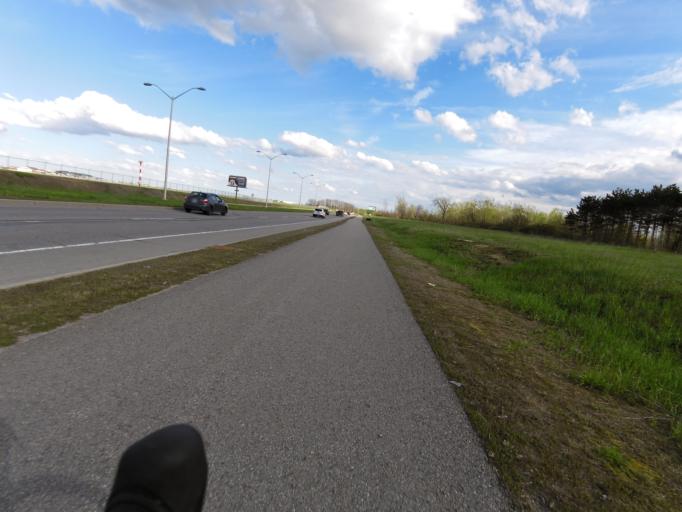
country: CA
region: Ontario
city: Ottawa
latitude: 45.3277
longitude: -75.6927
